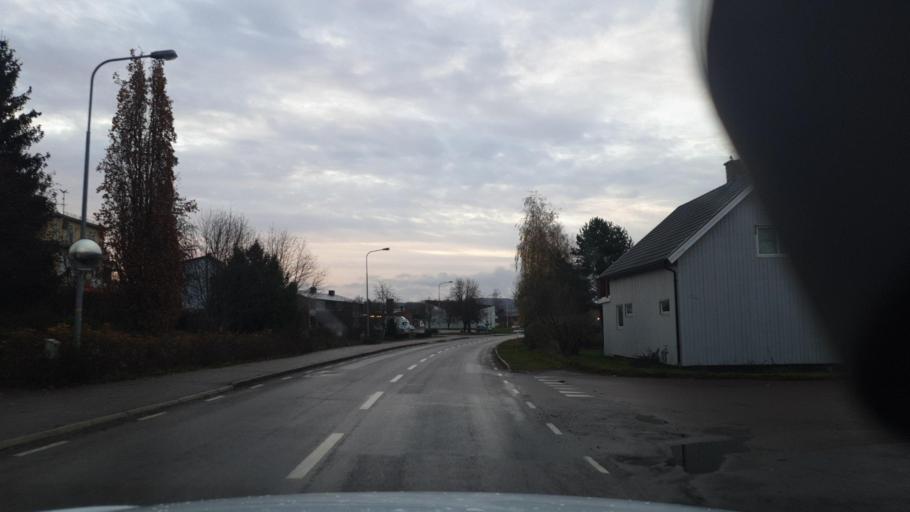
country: SE
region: Vaermland
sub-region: Eda Kommun
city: Amotfors
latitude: 59.7645
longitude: 12.3601
